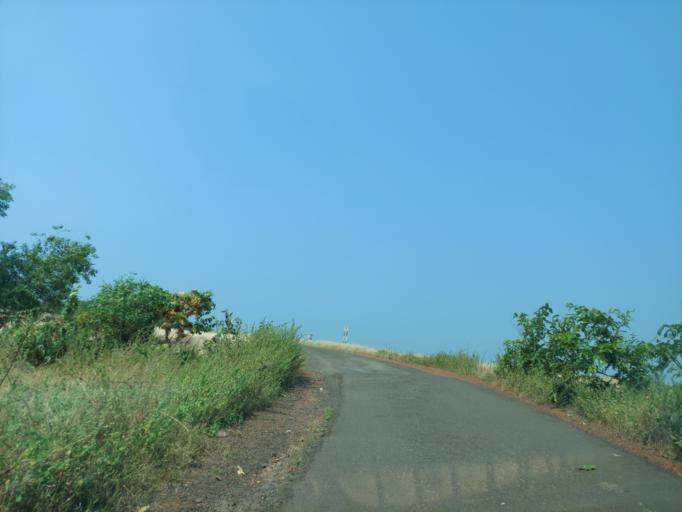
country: IN
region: Maharashtra
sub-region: Sindhudurg
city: Malvan
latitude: 15.9974
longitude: 73.5175
